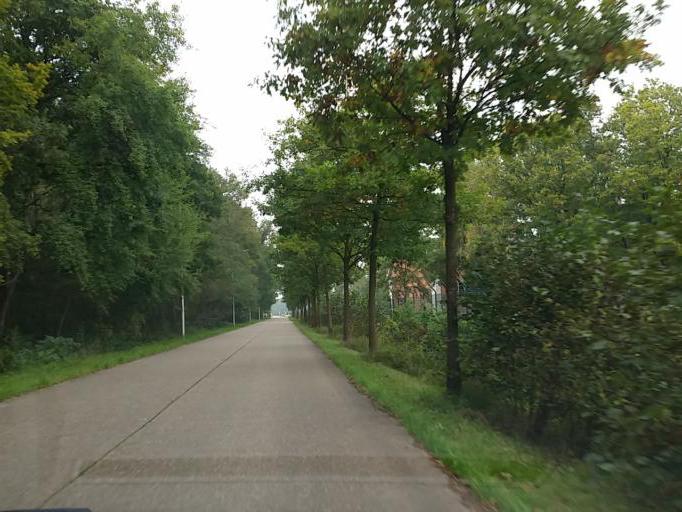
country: BE
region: Flanders
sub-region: Provincie Antwerpen
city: Brasschaat
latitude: 51.3331
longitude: 4.5039
